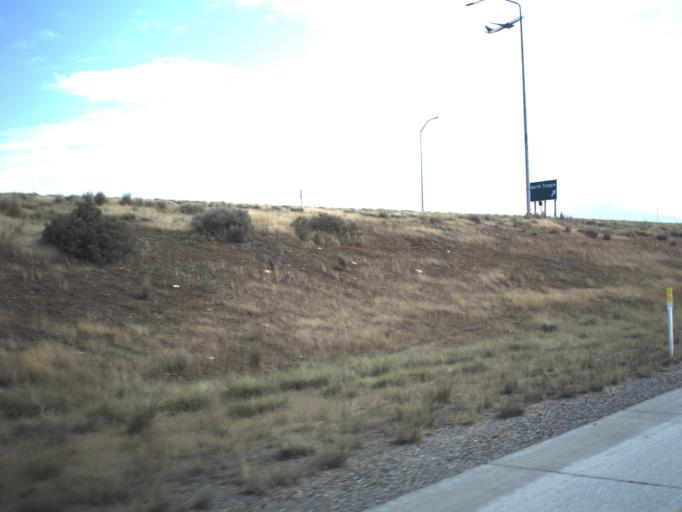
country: US
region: Utah
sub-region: Salt Lake County
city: West Valley City
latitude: 40.7632
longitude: -111.9810
